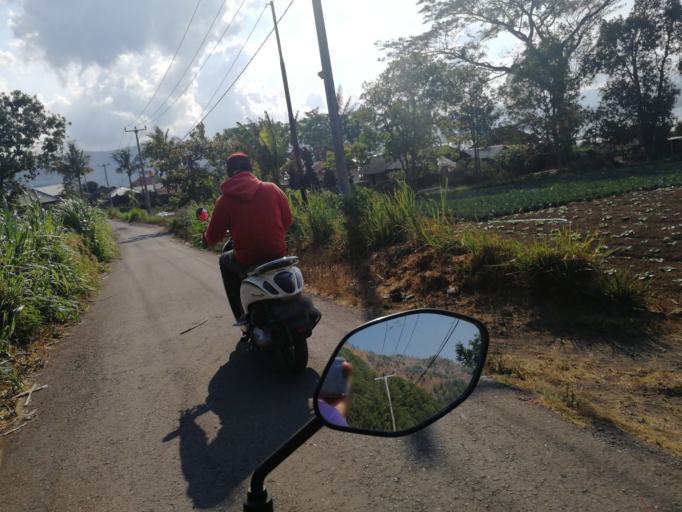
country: ID
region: Bali
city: Banjar Trunyan
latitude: -8.2706
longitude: 115.4165
